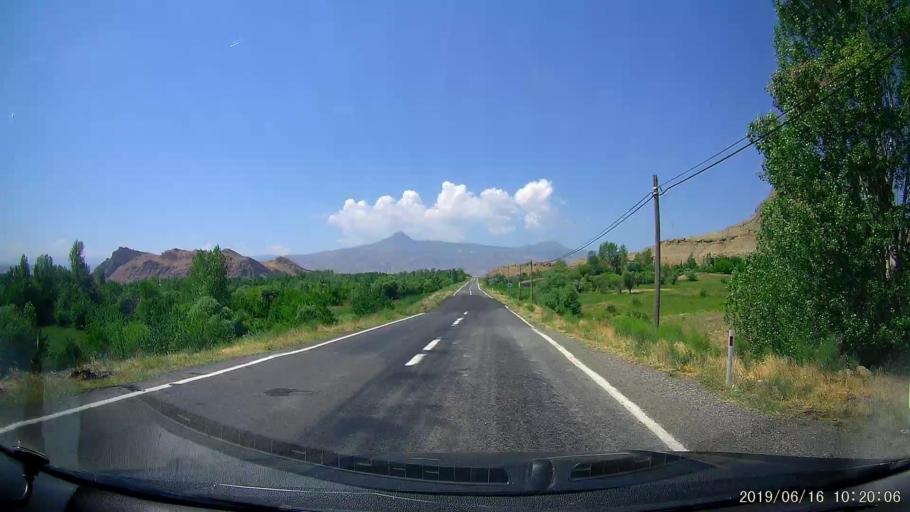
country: TR
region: Igdir
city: Tuzluca
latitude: 40.1505
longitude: 43.6508
